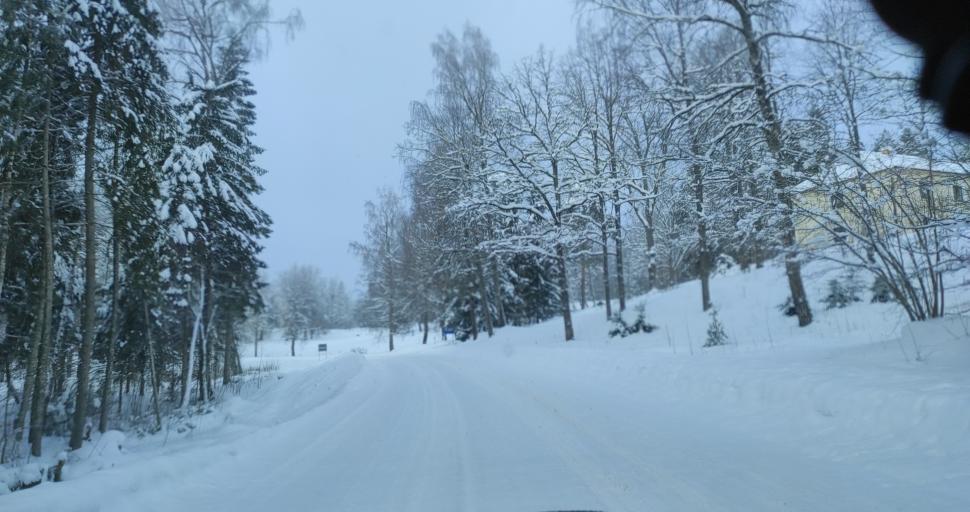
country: LV
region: Madonas Rajons
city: Madona
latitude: 56.8704
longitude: 25.9860
